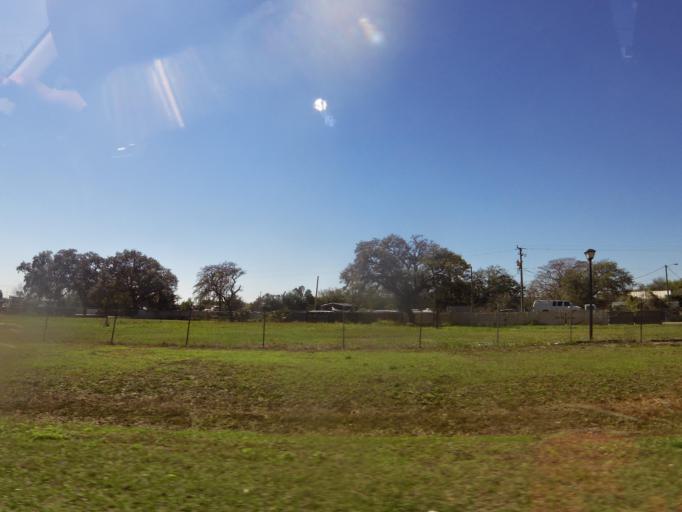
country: US
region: Florida
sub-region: Orange County
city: Lockhart
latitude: 28.6394
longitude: -81.4561
